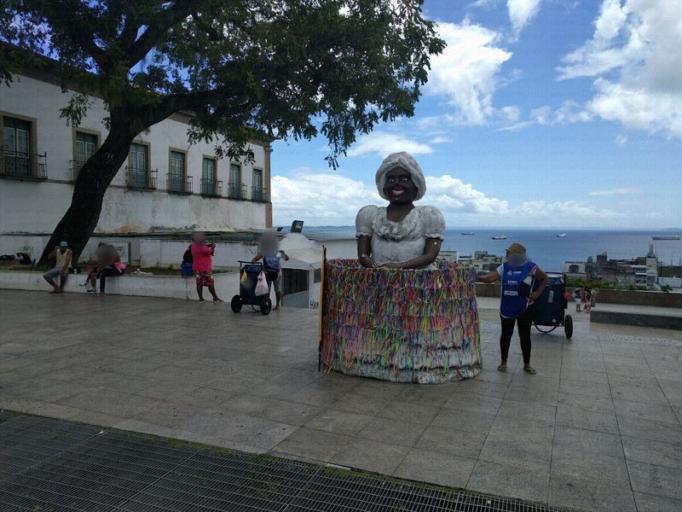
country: BR
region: Bahia
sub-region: Salvador
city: Salvador
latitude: -12.9735
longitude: -38.5117
